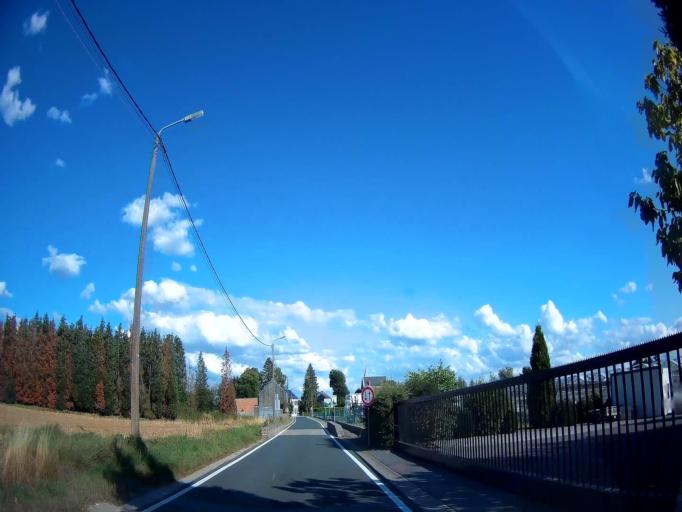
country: BE
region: Wallonia
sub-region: Province de Namur
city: Mettet
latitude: 50.3206
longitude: 4.7449
